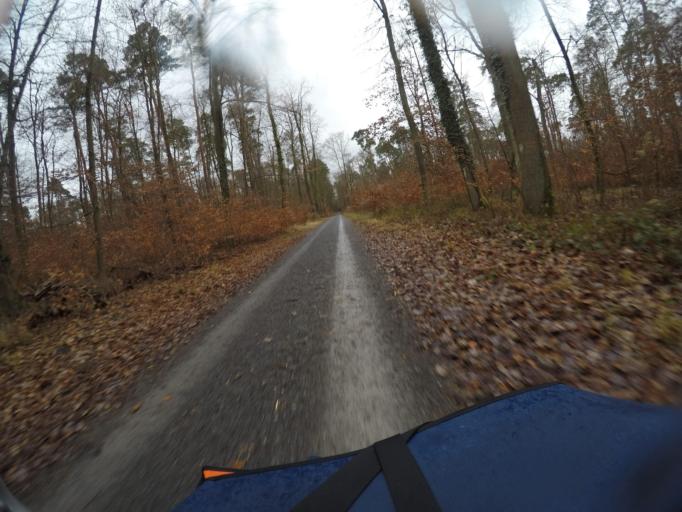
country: DE
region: Baden-Wuerttemberg
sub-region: Karlsruhe Region
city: Graben-Neudorf
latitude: 49.1407
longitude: 8.4573
